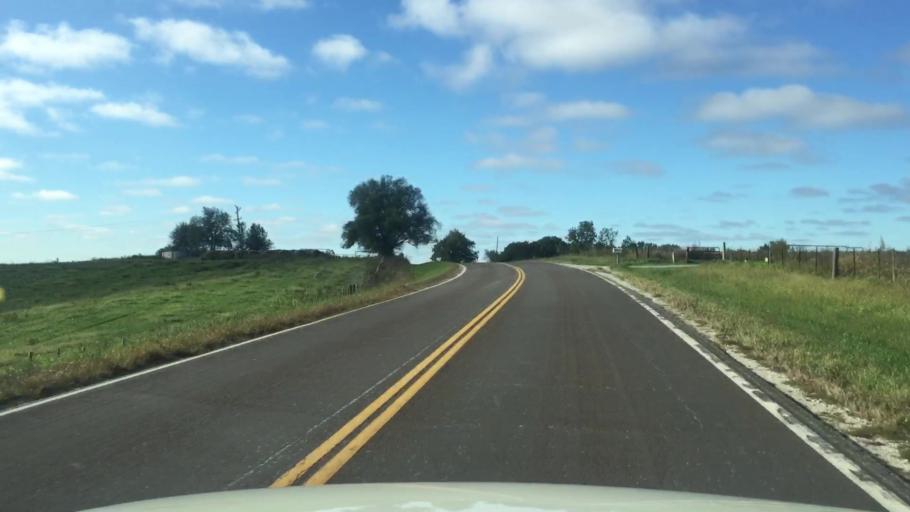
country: US
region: Missouri
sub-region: Howard County
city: Fayette
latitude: 39.0960
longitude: -92.7414
